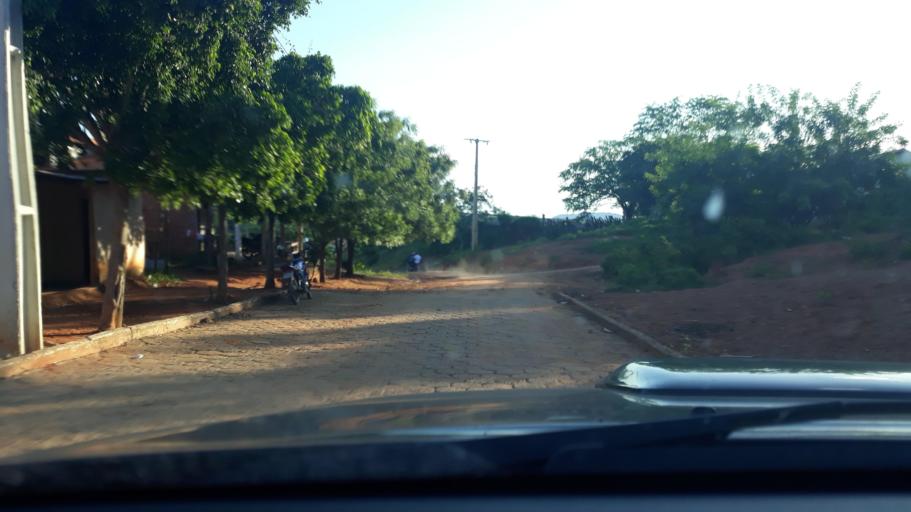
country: BR
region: Bahia
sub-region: Riacho De Santana
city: Riacho de Santana
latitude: -13.8260
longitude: -42.7272
